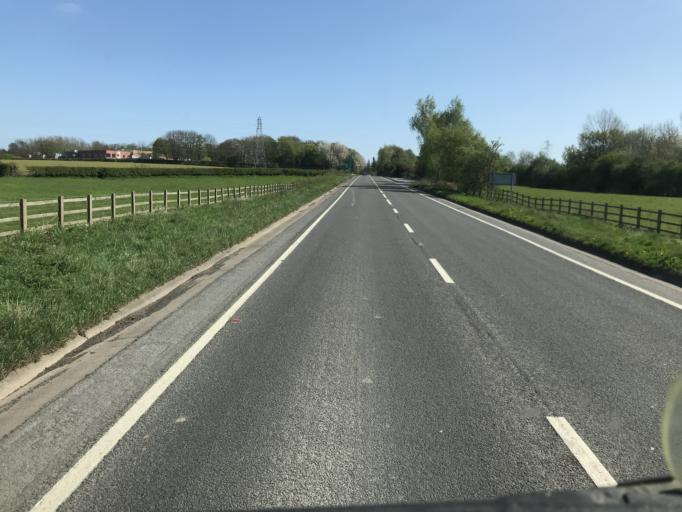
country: GB
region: England
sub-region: Cheshire East
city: Willaston
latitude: 53.0723
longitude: -2.4979
